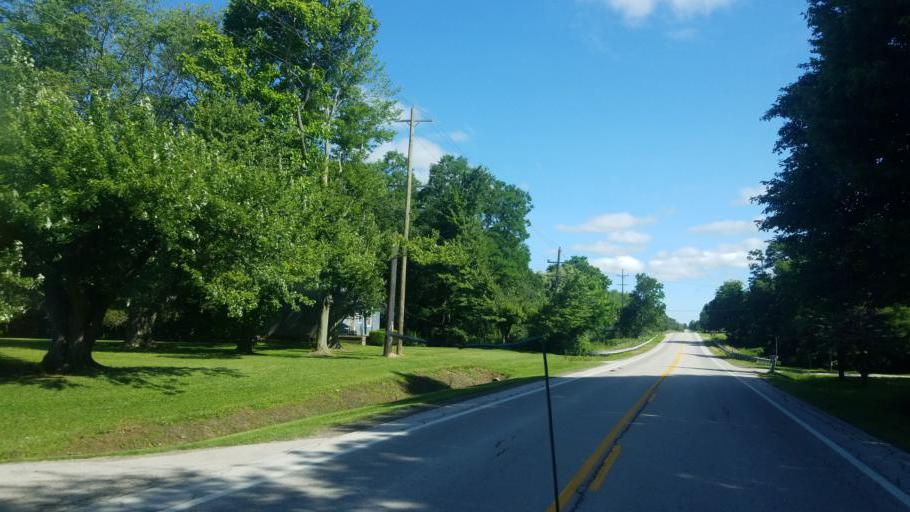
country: US
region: Ohio
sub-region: Ashtabula County
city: Conneaut
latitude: 41.8089
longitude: -80.5722
